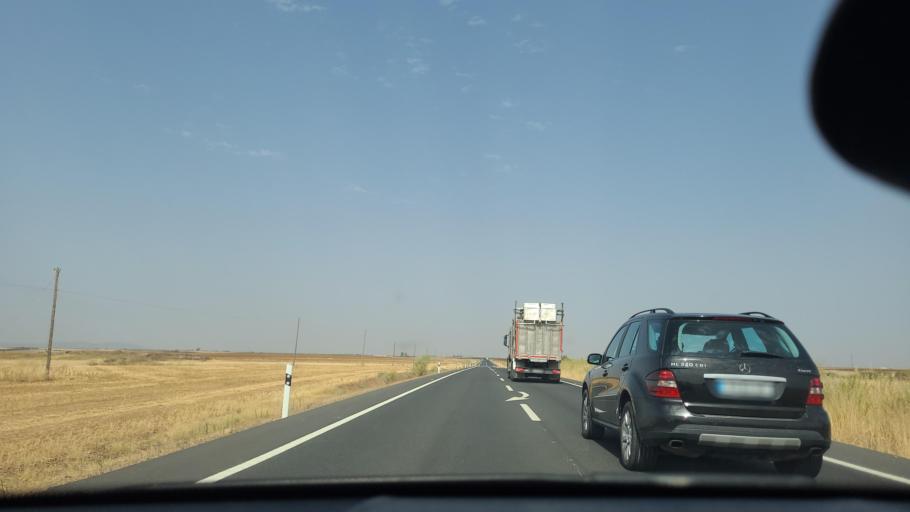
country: ES
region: Extremadura
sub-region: Provincia de Badajoz
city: Azuaga
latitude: 38.2604
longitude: -5.7236
